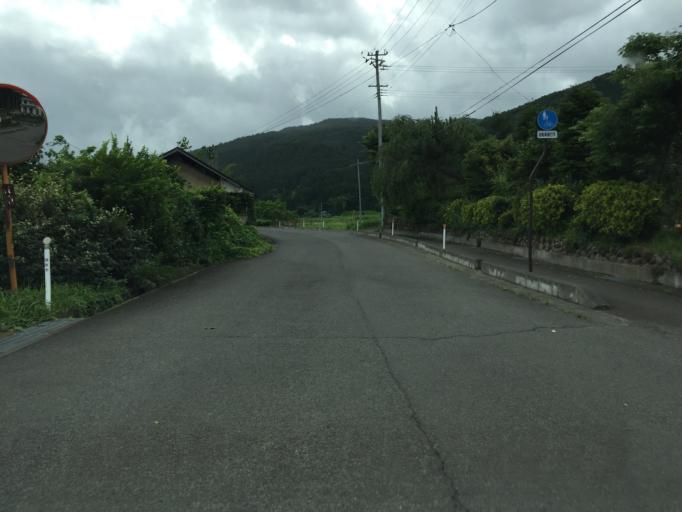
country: JP
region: Fukushima
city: Fukushima-shi
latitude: 37.7312
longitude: 140.3629
